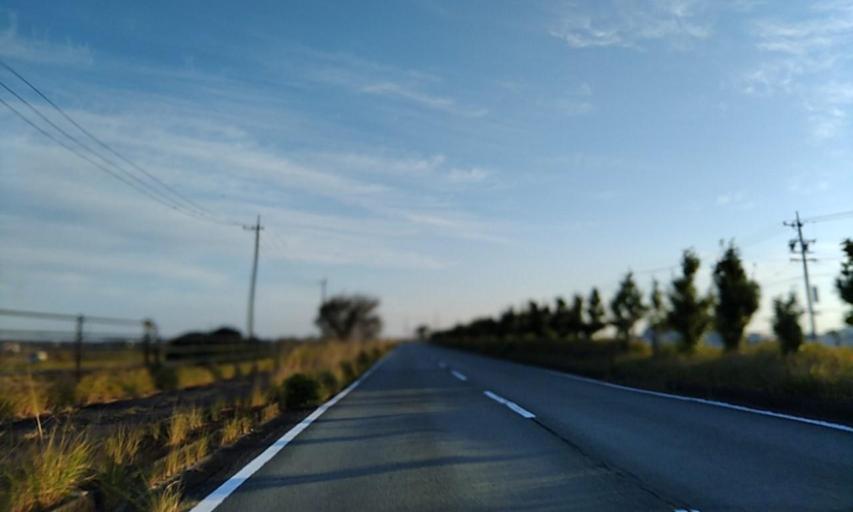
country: JP
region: Mie
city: Ise
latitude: 34.5019
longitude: 136.7488
